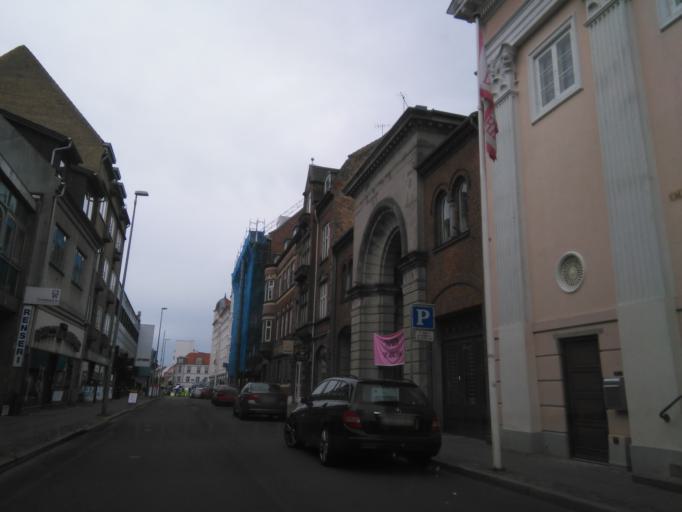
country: DK
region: Central Jutland
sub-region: Horsens Kommune
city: Horsens
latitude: 55.8615
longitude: 9.8544
